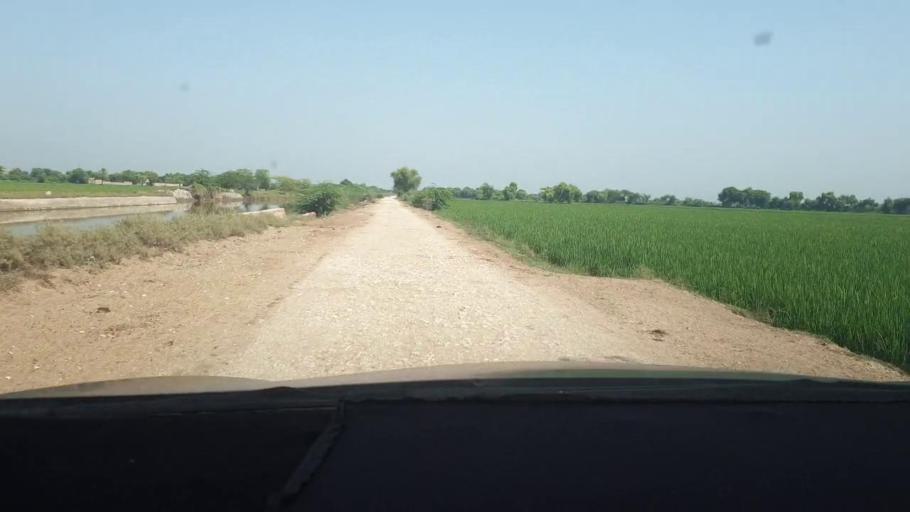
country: PK
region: Sindh
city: Miro Khan
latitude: 27.7048
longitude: 68.0780
